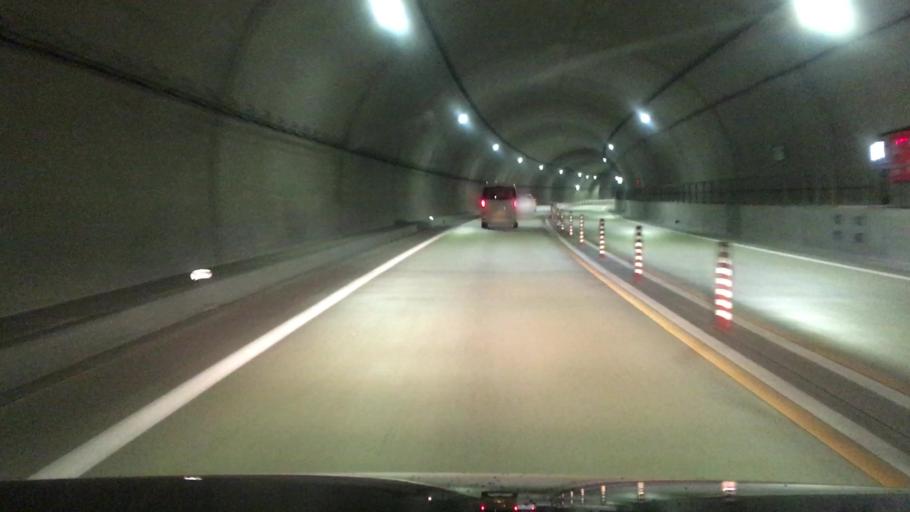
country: JP
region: Hyogo
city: Toyooka
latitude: 35.4123
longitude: 134.7450
